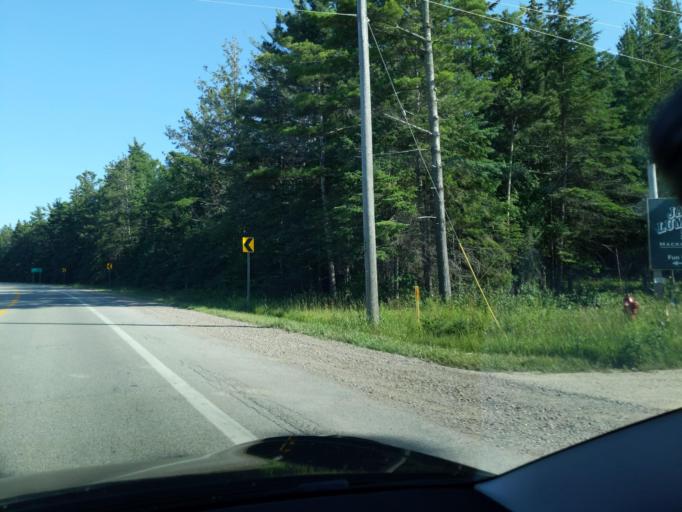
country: US
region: Michigan
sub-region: Mackinac County
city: Saint Ignace
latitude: 45.7673
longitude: -84.7246
